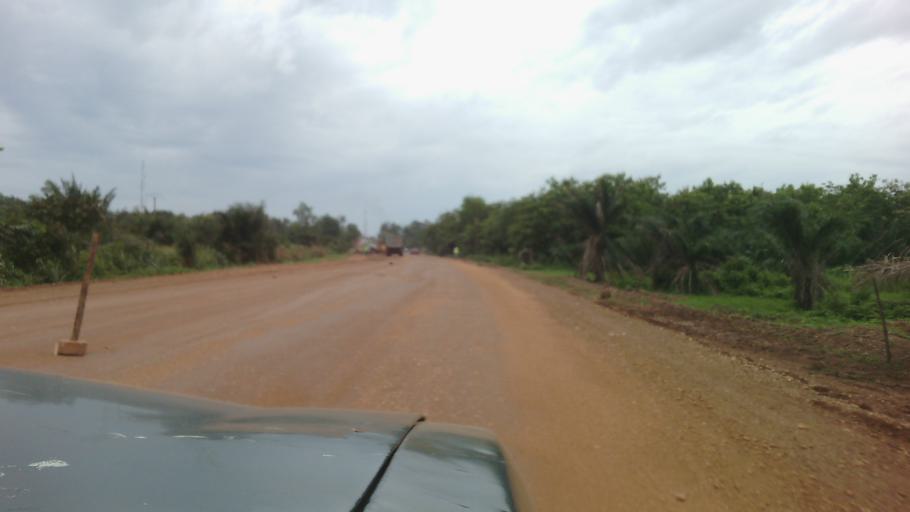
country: BJ
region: Mono
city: Lokossa
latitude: 6.5666
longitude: 1.8006
